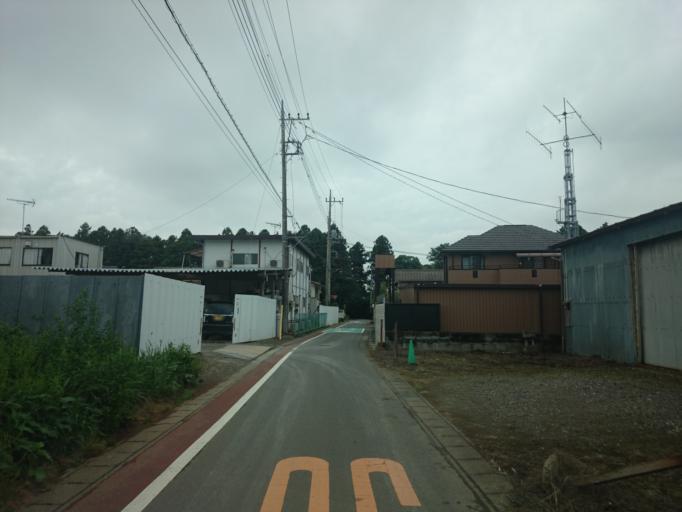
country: JP
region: Ibaraki
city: Tsukuba
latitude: 36.1118
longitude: 140.0792
